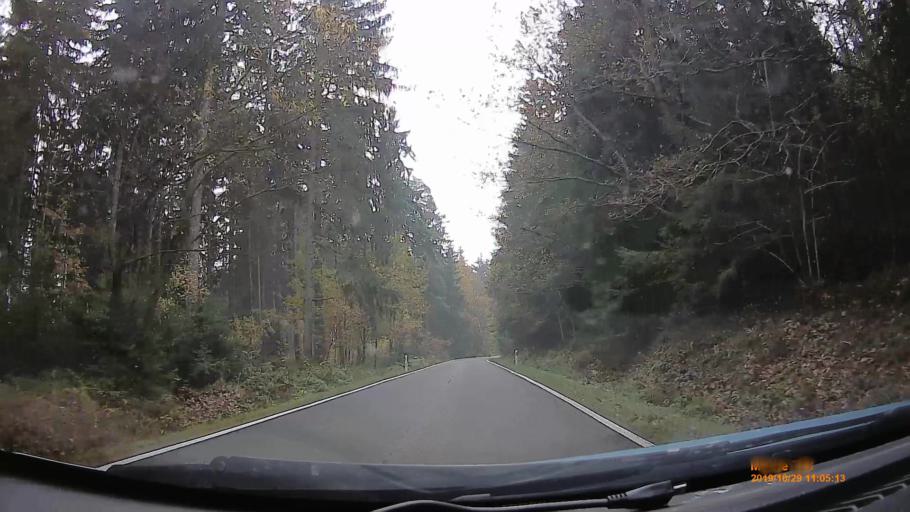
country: PL
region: Lower Silesian Voivodeship
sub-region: Powiat klodzki
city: Szczytna
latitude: 50.4727
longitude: 16.4741
